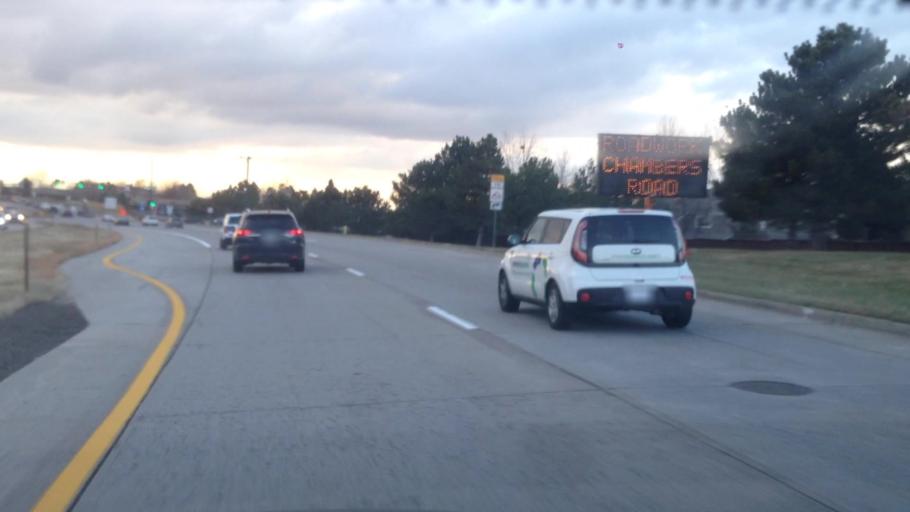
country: US
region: Colorado
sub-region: Douglas County
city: Stonegate
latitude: 39.5364
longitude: -104.8097
